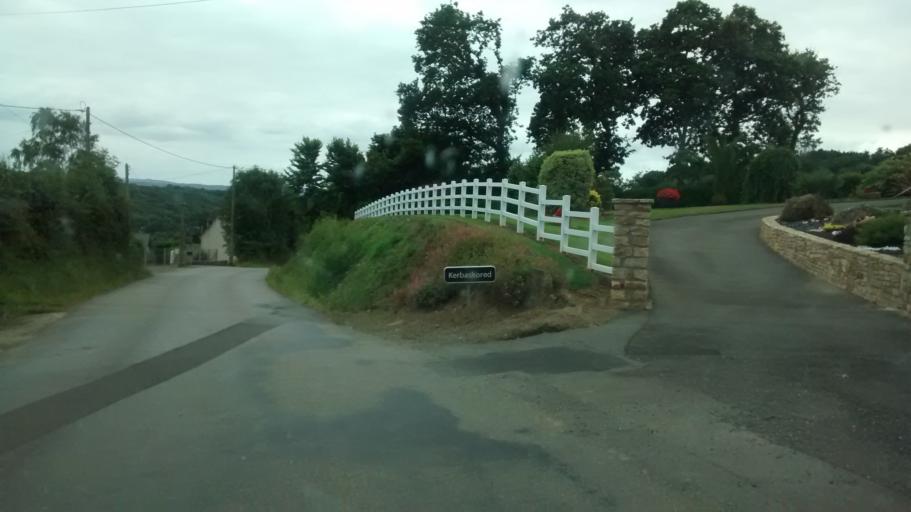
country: FR
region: Brittany
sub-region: Departement du Finistere
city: Plougastel-Daoulas
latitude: 48.3542
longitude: -4.3897
